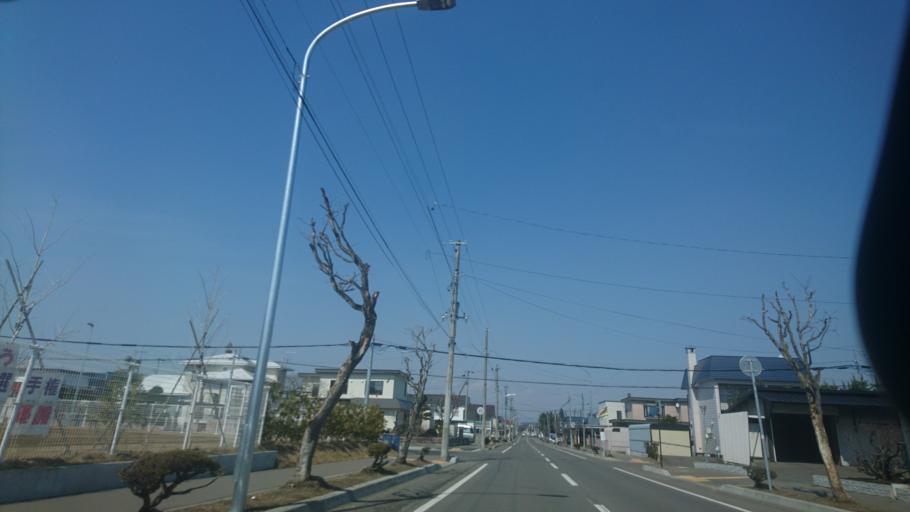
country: JP
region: Hokkaido
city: Obihiro
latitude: 42.9133
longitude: 143.0589
